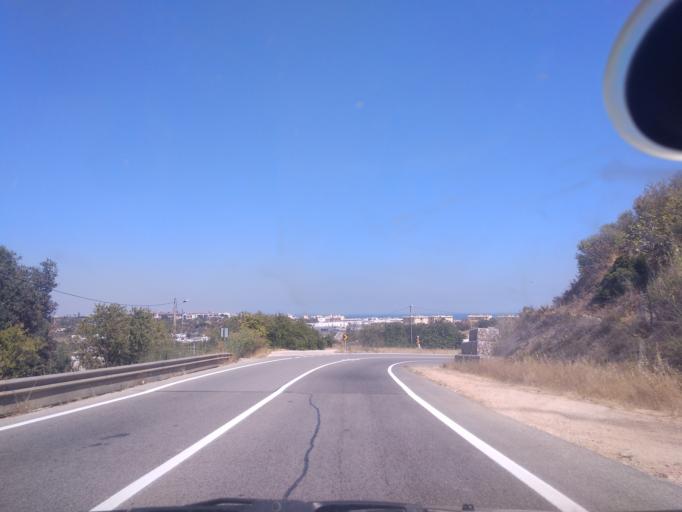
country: PT
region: Faro
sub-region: Lagos
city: Lagos
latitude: 37.1160
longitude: -8.6873
